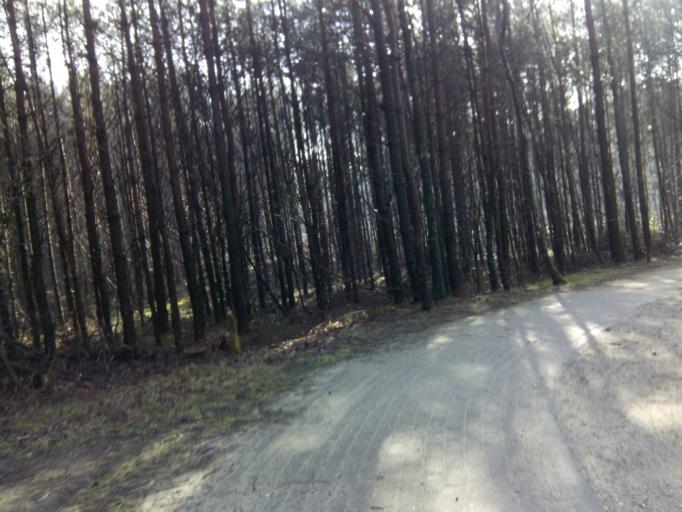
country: NL
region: Utrecht
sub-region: Gemeente Utrechtse Heuvelrug
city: Leersum
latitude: 52.0134
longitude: 5.4454
